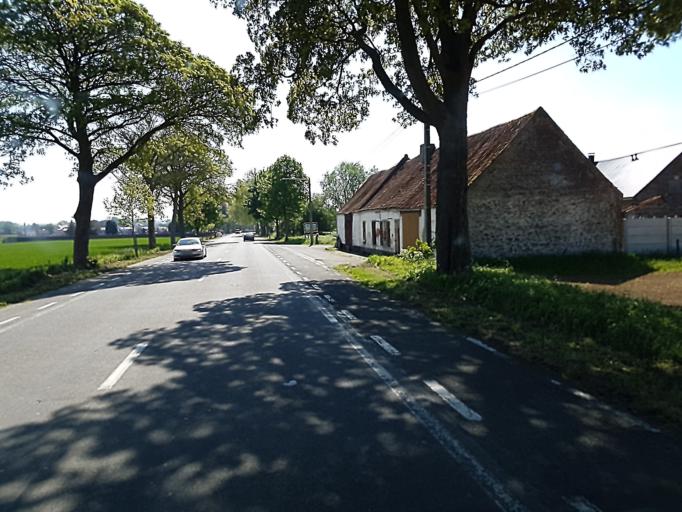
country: BE
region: Wallonia
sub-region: Province du Hainaut
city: Lens
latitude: 50.5632
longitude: 3.8907
